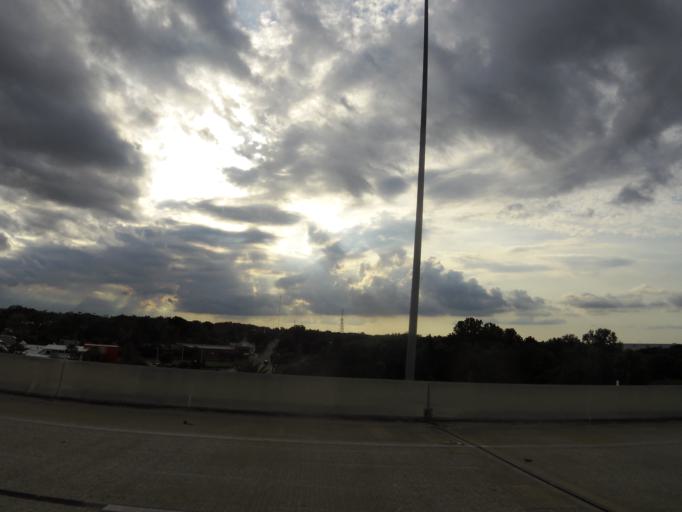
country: US
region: Florida
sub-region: Duval County
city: Jacksonville
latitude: 30.3239
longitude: -81.6814
